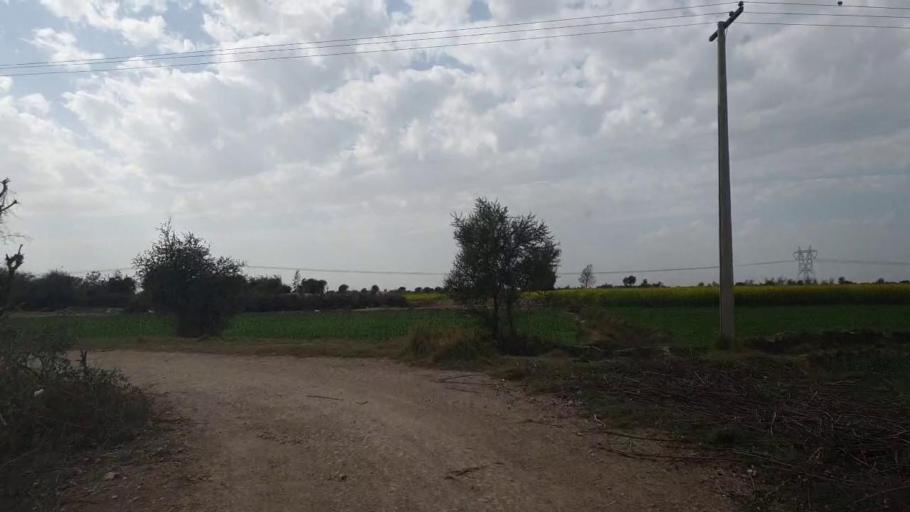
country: PK
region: Sindh
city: Hala
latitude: 25.9350
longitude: 68.4536
